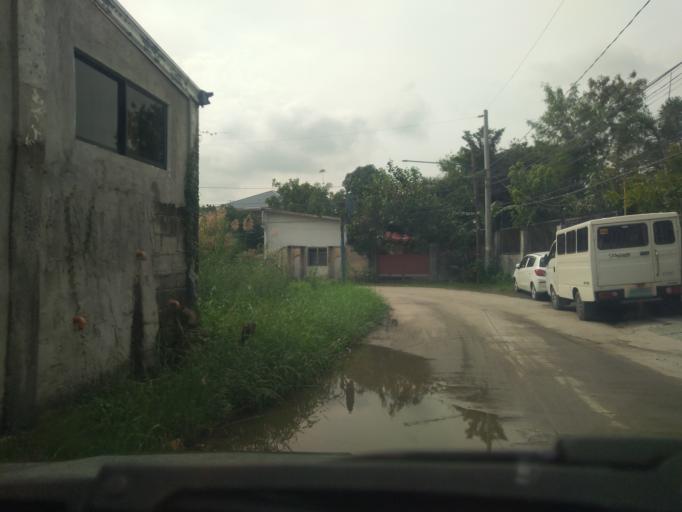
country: PH
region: Central Luzon
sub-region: Province of Pampanga
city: Pau
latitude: 15.0053
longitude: 120.7125
